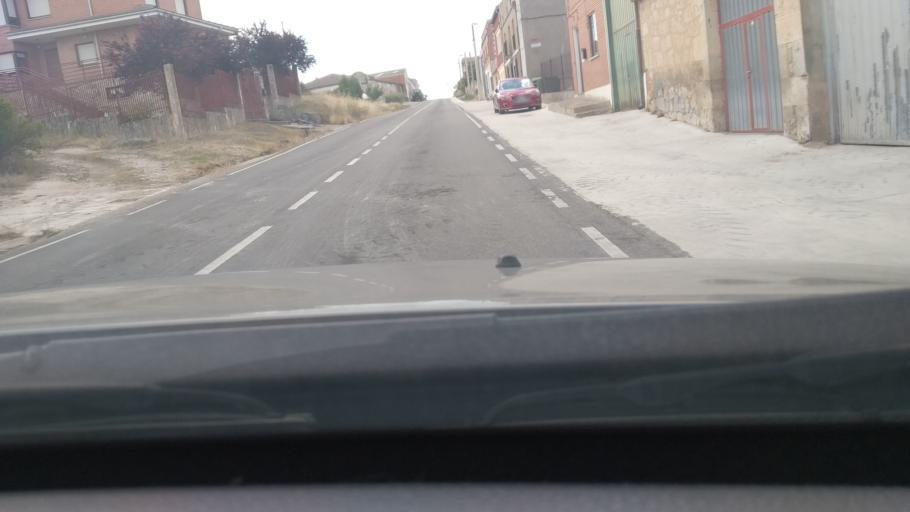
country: ES
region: Castille and Leon
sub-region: Provincia de Burgos
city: Villafruela
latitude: 41.9174
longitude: -3.9103
